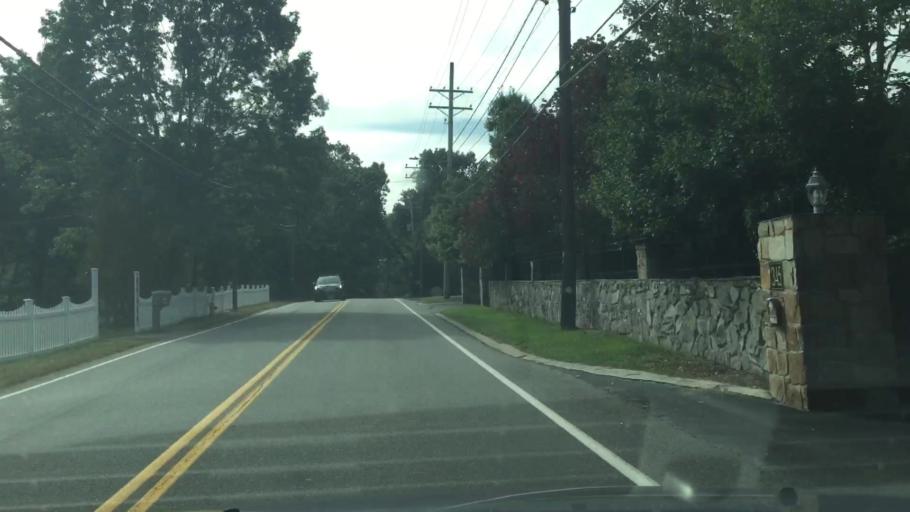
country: US
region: Massachusetts
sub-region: Middlesex County
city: Tewksbury
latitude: 42.6698
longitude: -71.2322
